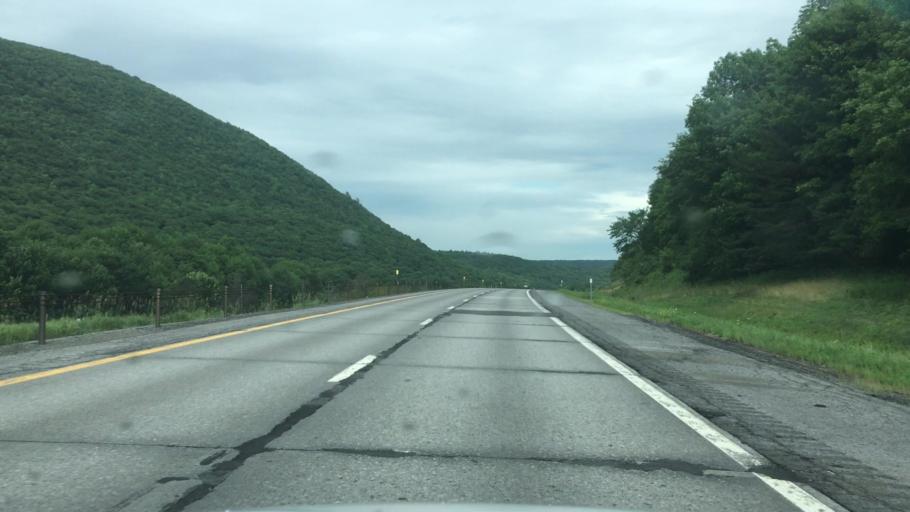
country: US
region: New York
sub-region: Otsego County
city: Worcester
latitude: 42.6448
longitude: -74.6456
